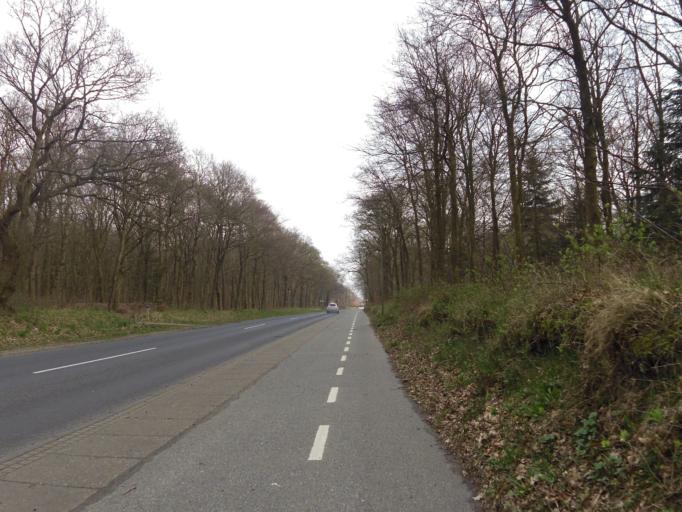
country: DK
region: South Denmark
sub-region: Esbjerg Kommune
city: Ribe
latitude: 55.3399
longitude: 8.7673
